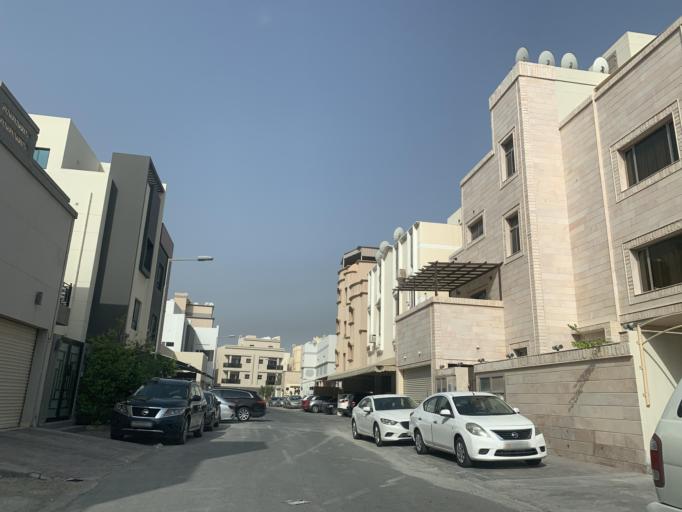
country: BH
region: Northern
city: Madinat `Isa
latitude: 26.1872
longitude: 50.5657
